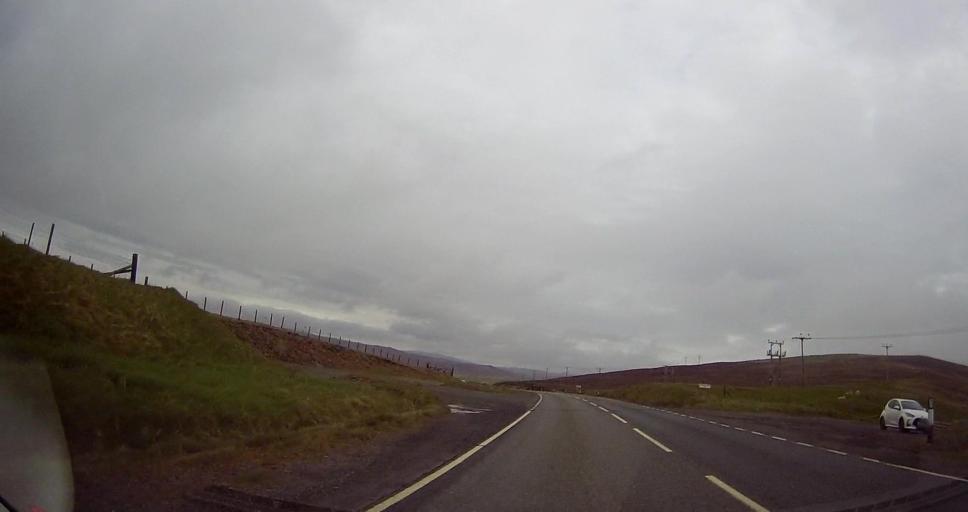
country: GB
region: Scotland
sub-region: Shetland Islands
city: Lerwick
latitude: 60.1754
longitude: -1.2229
